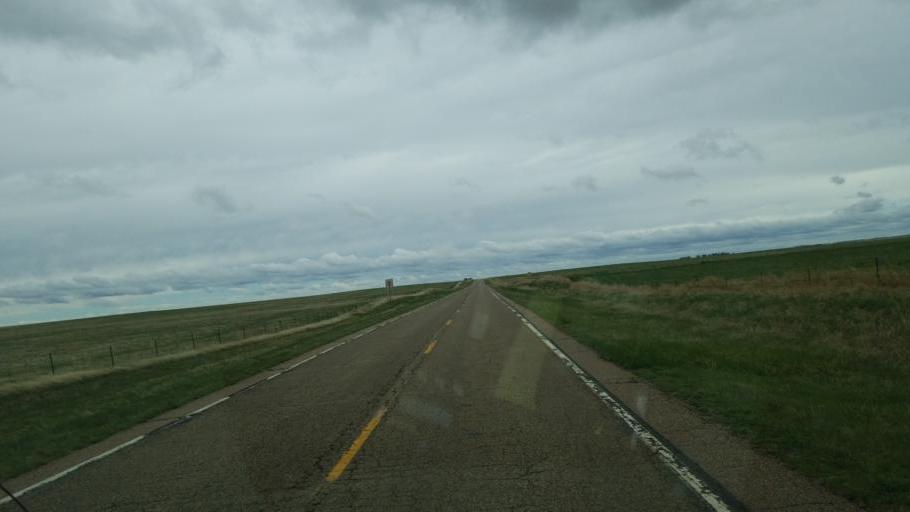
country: US
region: Colorado
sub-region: Lincoln County
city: Hugo
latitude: 38.8521
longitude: -103.7081
